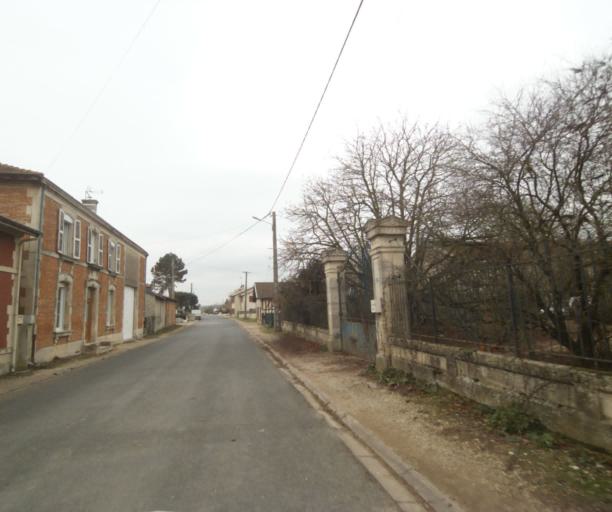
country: FR
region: Champagne-Ardenne
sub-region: Departement de la Haute-Marne
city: Villiers-en-Lieu
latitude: 48.6420
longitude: 4.8702
